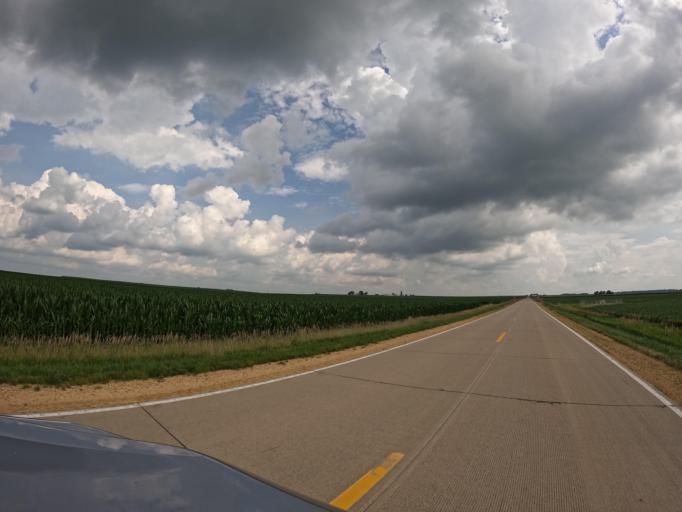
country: US
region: Iowa
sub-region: Clinton County
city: De Witt
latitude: 41.7909
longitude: -90.4132
